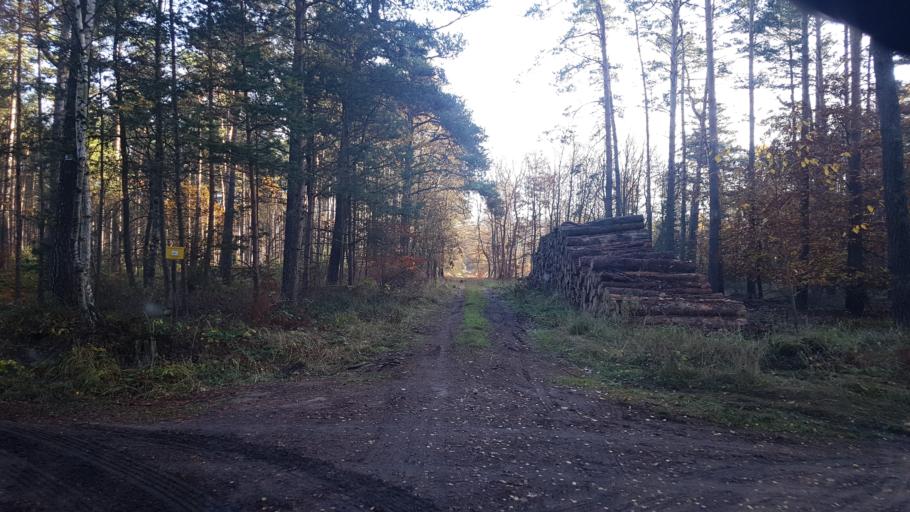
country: DE
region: Brandenburg
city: Crinitz
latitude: 51.7104
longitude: 13.7430
